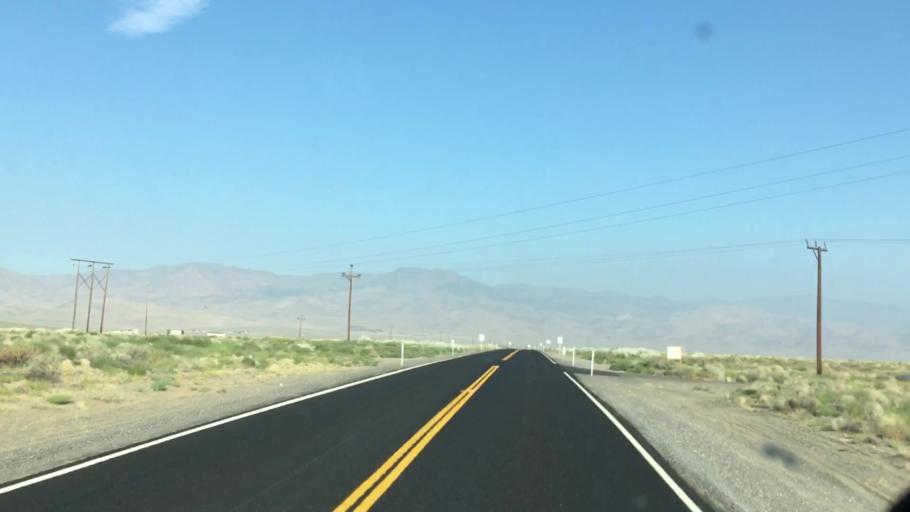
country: US
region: Nevada
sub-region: Lyon County
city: Fernley
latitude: 39.6409
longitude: -119.2986
